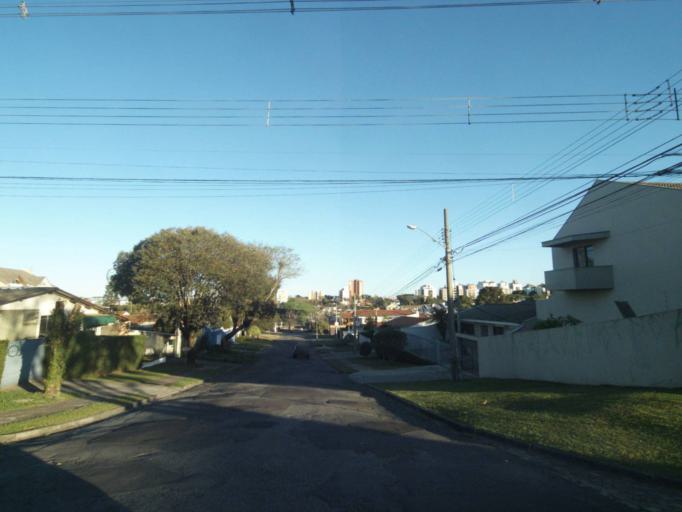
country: BR
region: Parana
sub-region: Curitiba
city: Curitiba
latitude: -25.3905
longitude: -49.2484
